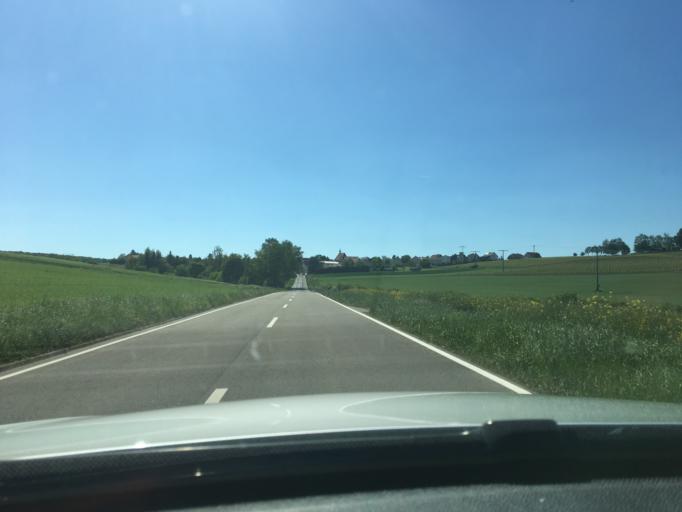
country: DE
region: Rheinland-Pfalz
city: Bechenheim
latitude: 49.7301
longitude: 8.0139
